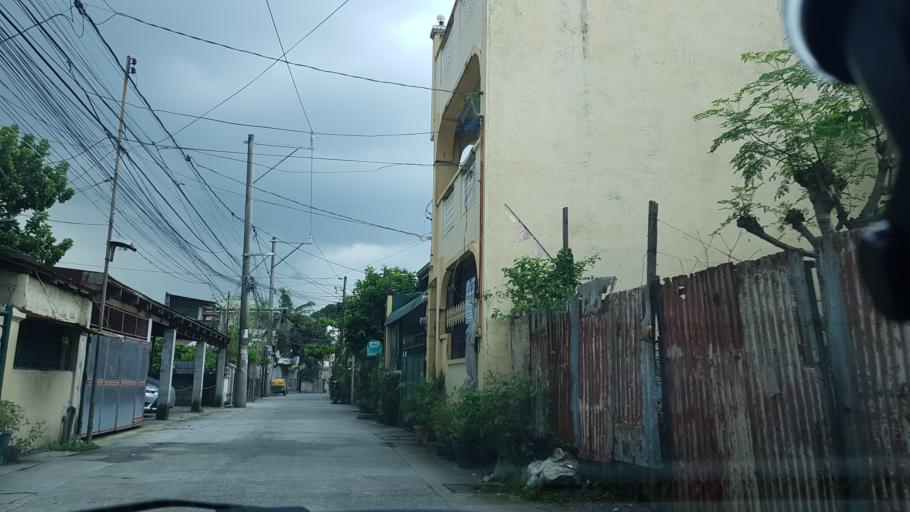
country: PH
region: Calabarzon
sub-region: Province of Rizal
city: Pateros
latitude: 14.5331
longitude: 121.0703
